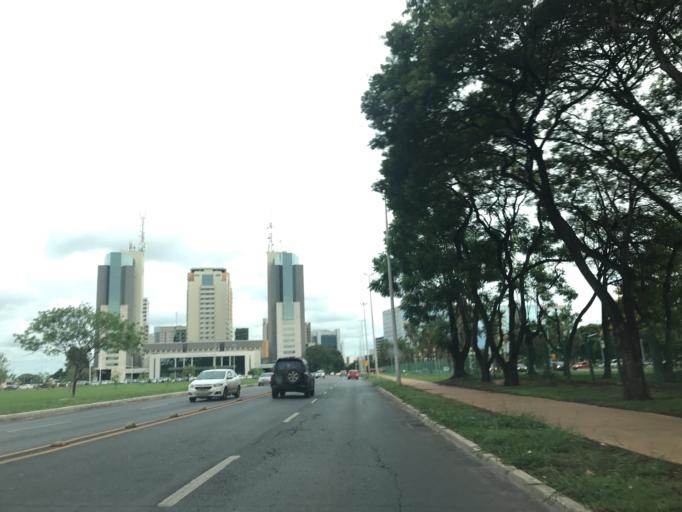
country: BR
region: Federal District
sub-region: Brasilia
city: Brasilia
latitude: -15.7918
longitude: -47.8970
